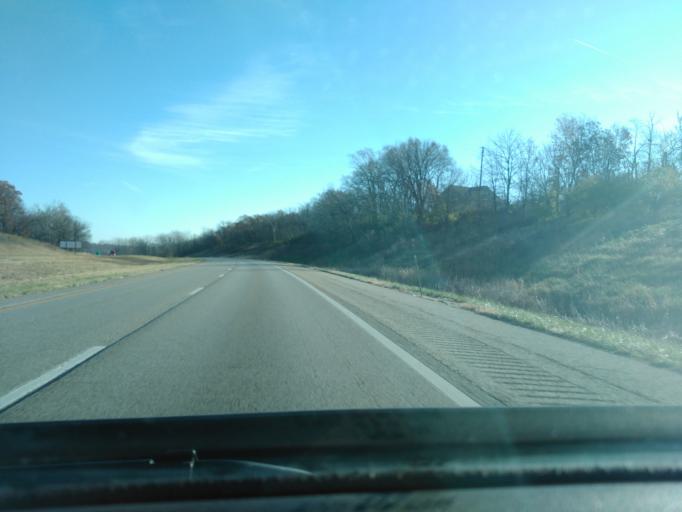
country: US
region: Illinois
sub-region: Bond County
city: Greenville
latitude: 38.8326
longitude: -89.5158
